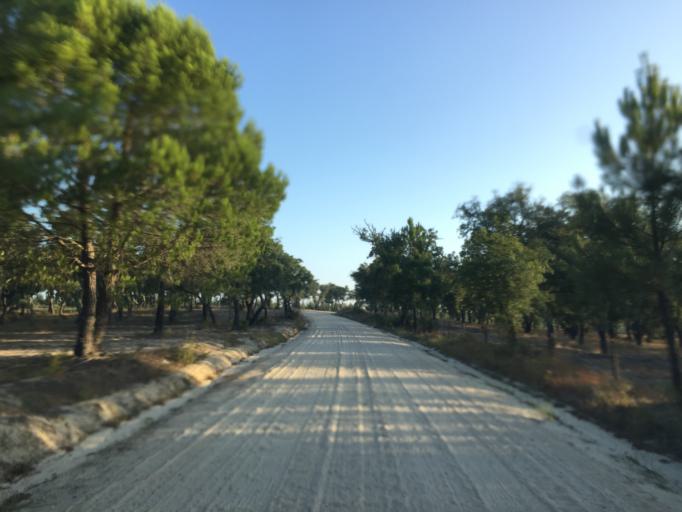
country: PT
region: Portalegre
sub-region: Ponte de Sor
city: Santo Andre
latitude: 39.0858
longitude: -8.3823
